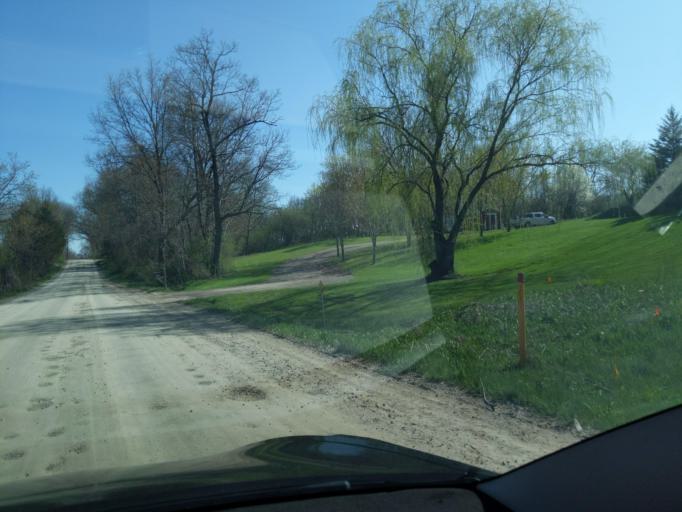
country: US
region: Michigan
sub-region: Washtenaw County
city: Chelsea
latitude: 42.4048
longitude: -84.0837
